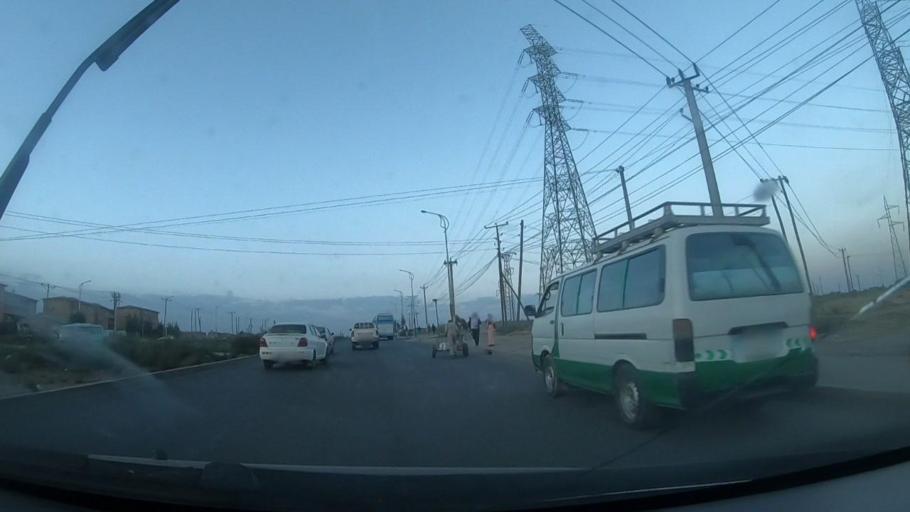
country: ET
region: Adis Abeba
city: Addis Ababa
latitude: 9.0424
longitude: 38.8779
